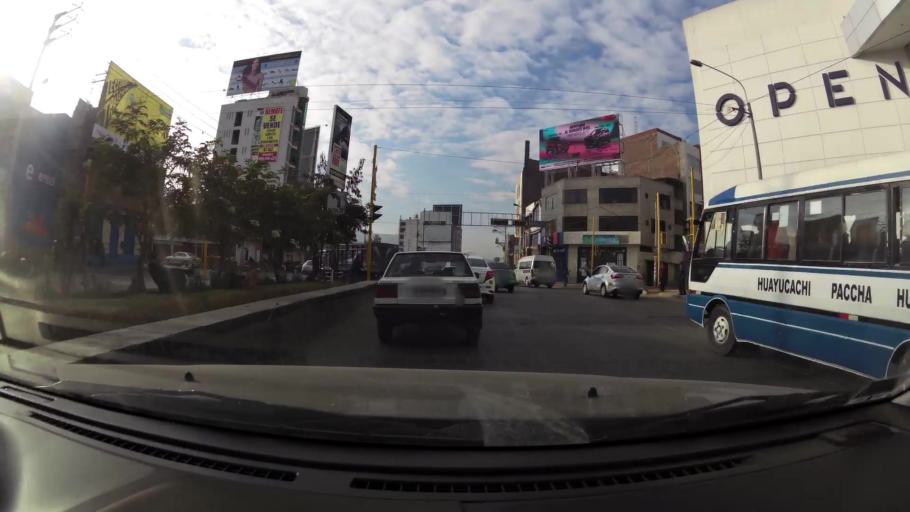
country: PE
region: Junin
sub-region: Provincia de Huancayo
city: Huancayo
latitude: -12.0619
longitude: -75.2089
